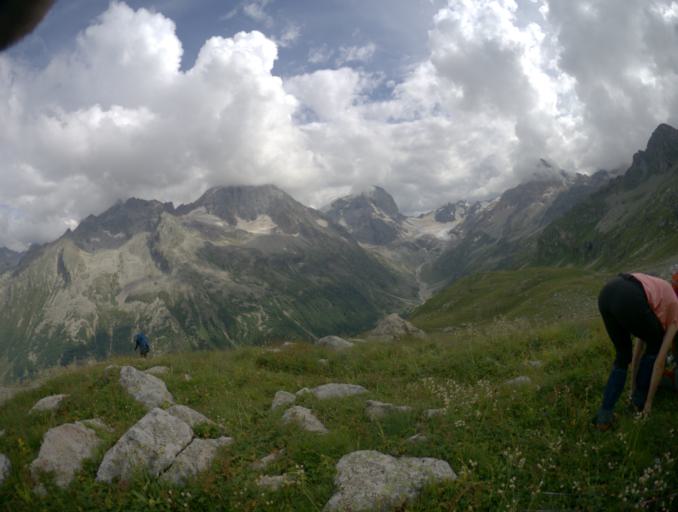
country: RU
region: Karachayevo-Cherkesiya
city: Uchkulan
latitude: 43.2697
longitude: 42.1273
